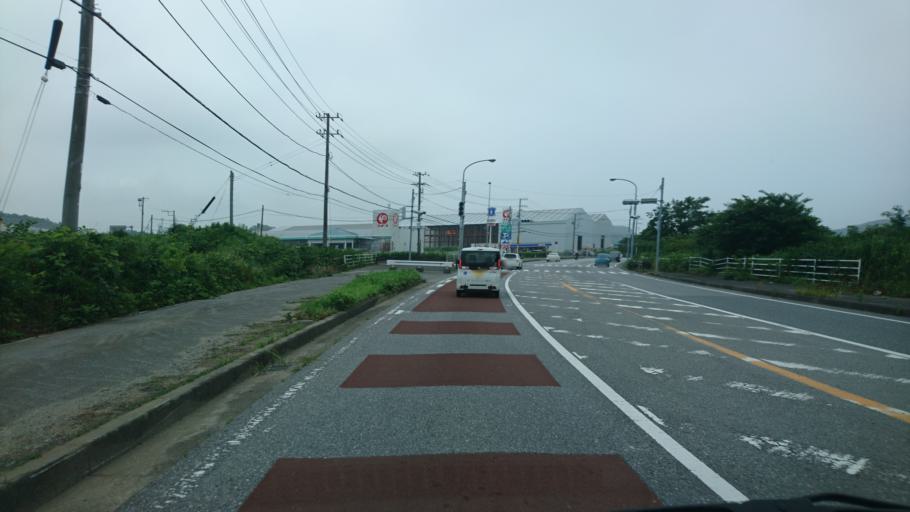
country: JP
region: Chiba
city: Kimitsu
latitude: 35.2368
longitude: 139.8875
